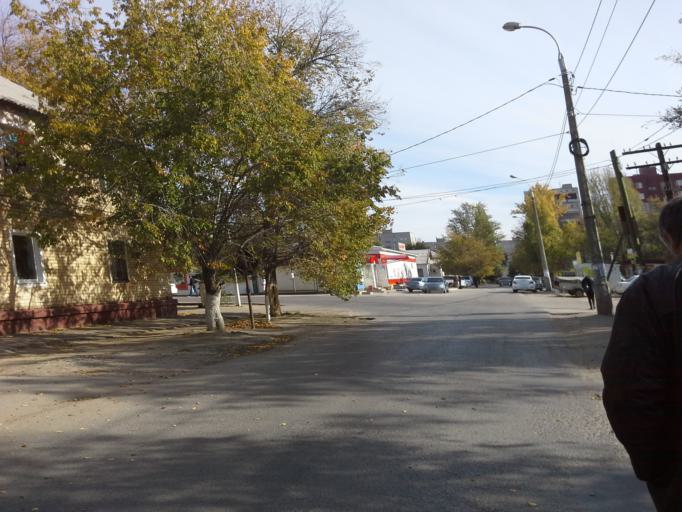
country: RU
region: Volgograd
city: Vodstroy
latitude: 48.8410
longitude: 44.6400
